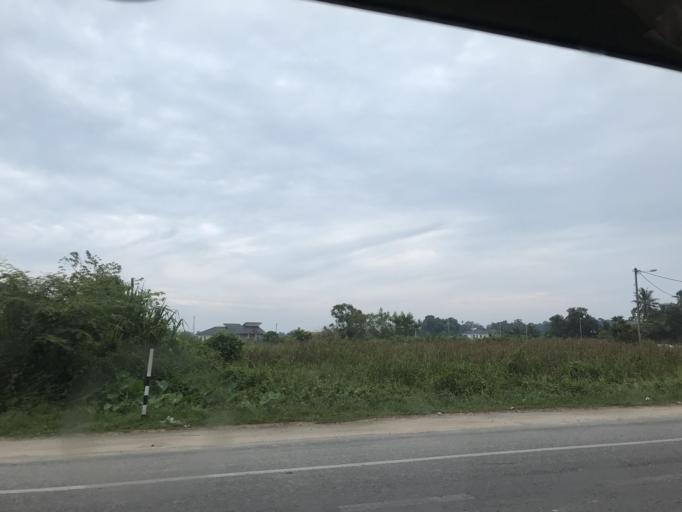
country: MY
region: Kelantan
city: Kota Bharu
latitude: 6.1461
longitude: 102.2201
